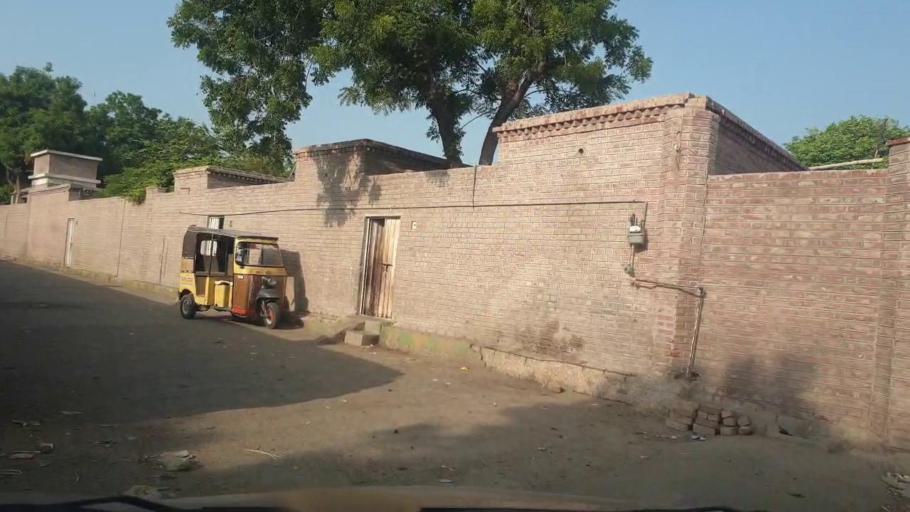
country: PK
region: Sindh
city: Larkana
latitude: 27.5787
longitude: 68.1771
